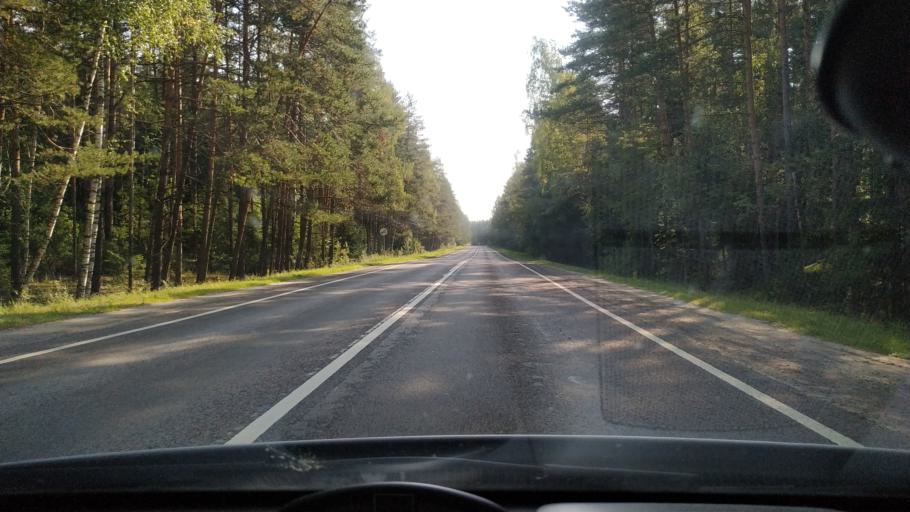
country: RU
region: Moskovskaya
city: Dmitrovskiy Pogost
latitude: 55.2359
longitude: 39.9647
